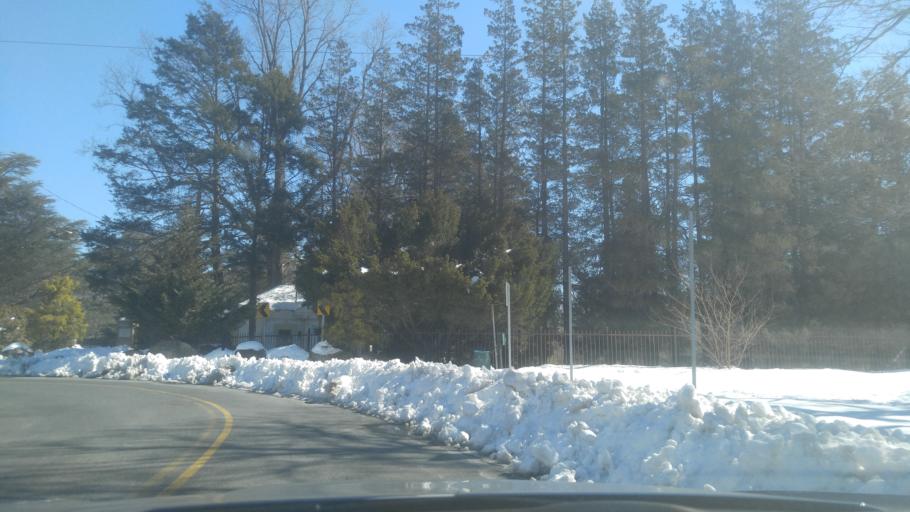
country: US
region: Rhode Island
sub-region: Providence County
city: Pawtucket
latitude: 41.8578
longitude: -71.3842
